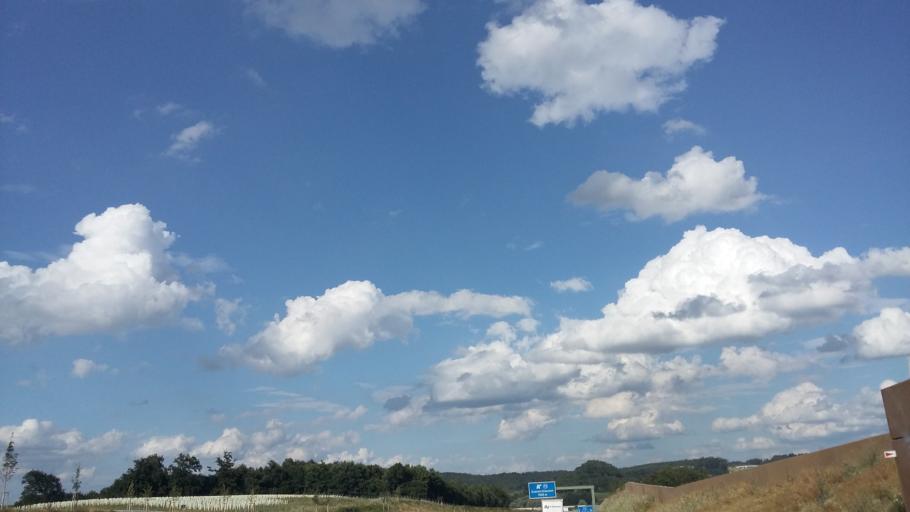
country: DE
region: Bavaria
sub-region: Swabia
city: Zusmarshausen
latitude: 48.4076
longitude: 10.5775
